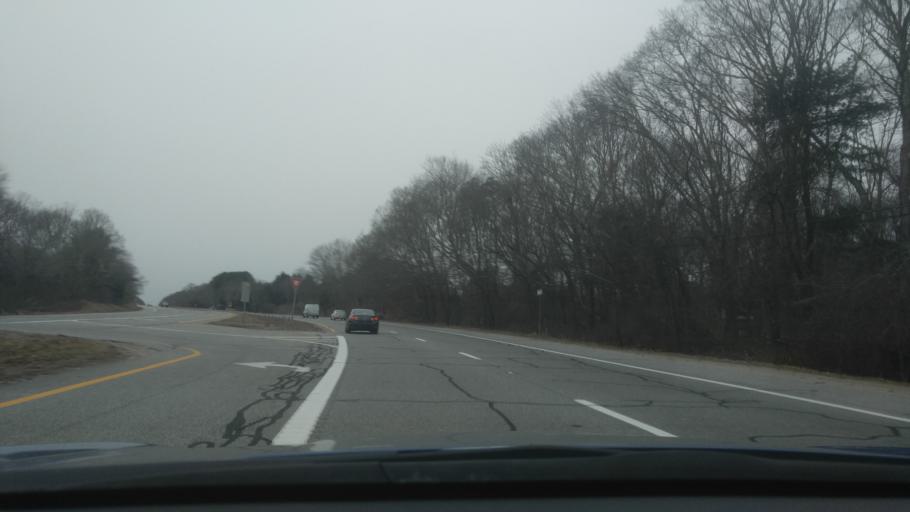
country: US
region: Rhode Island
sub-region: Washington County
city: Wakefield-Peacedale
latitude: 41.4259
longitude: -71.5233
